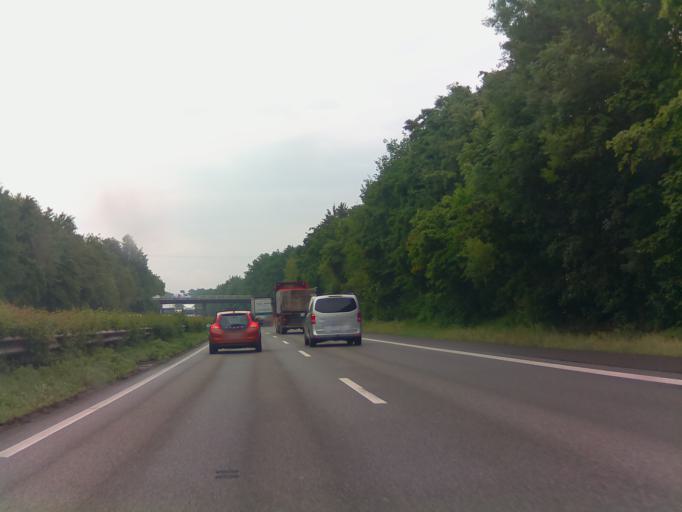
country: DE
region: Rheinland-Pfalz
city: Lingenfeld
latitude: 49.2524
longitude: 8.3315
